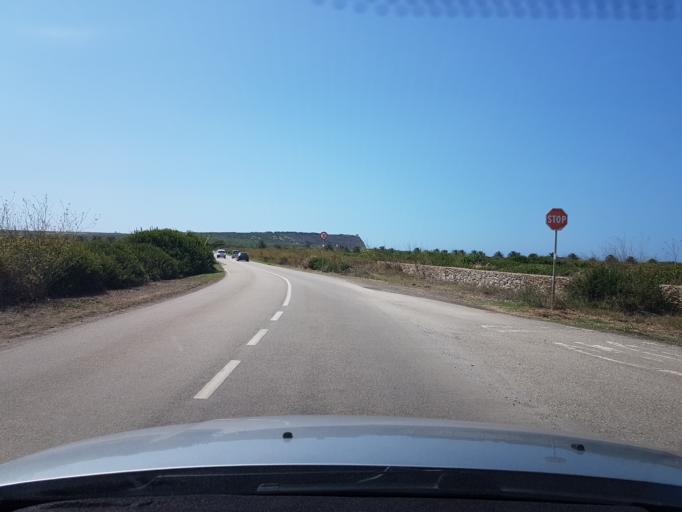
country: IT
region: Sardinia
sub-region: Provincia di Oristano
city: Riola Sardo
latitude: 40.0407
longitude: 8.4055
